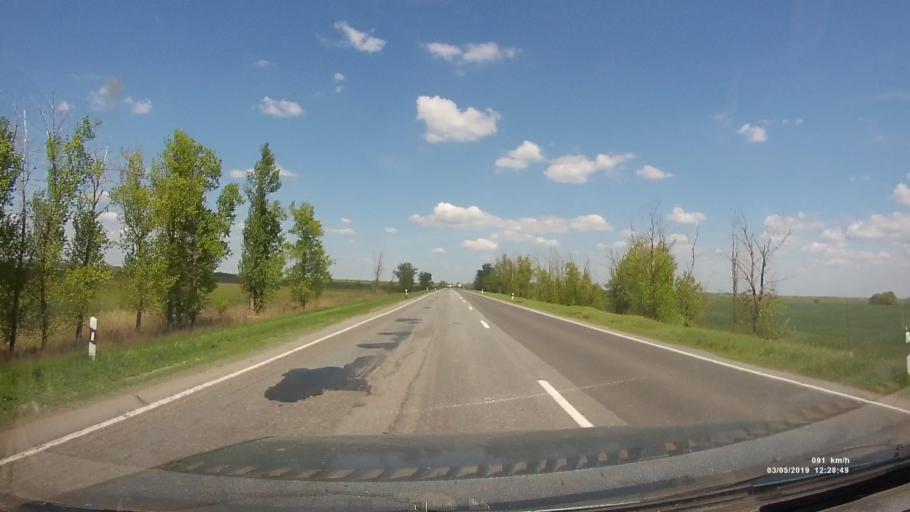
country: RU
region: Rostov
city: Semikarakorsk
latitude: 47.4787
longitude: 40.7310
